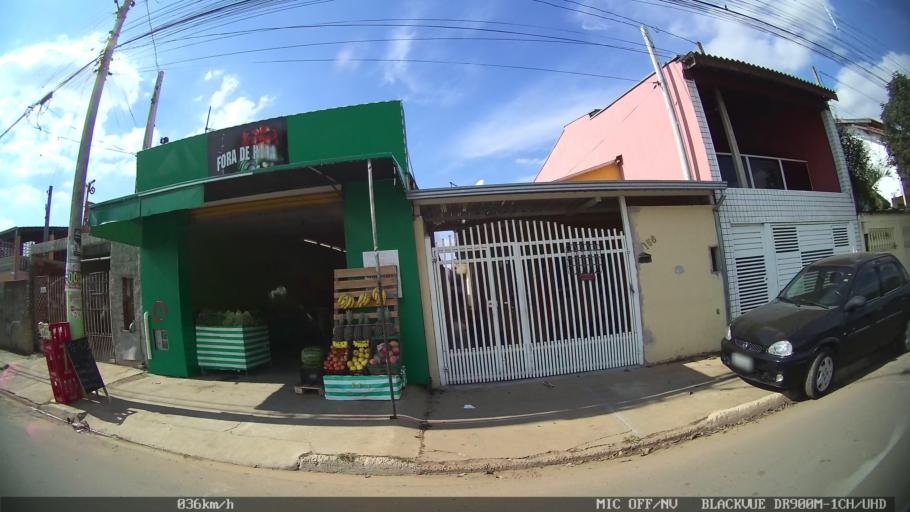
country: BR
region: Sao Paulo
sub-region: Hortolandia
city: Hortolandia
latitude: -22.9020
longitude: -47.2509
